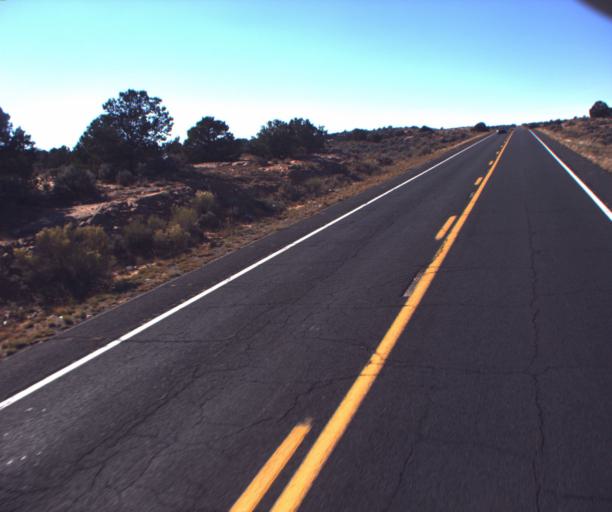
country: US
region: Arizona
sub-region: Coconino County
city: Kaibito
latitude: 36.5778
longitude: -110.7791
